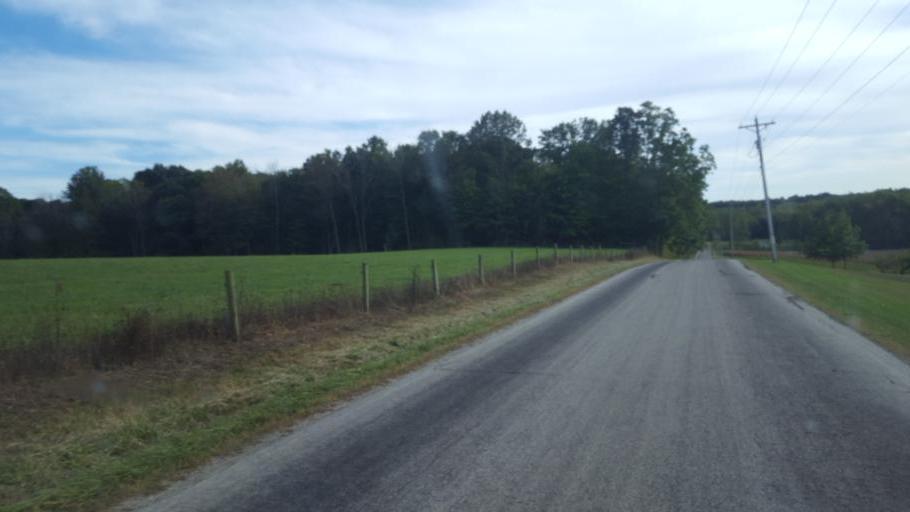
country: US
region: Ohio
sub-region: Knox County
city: Fredericktown
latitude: 40.5630
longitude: -82.6047
